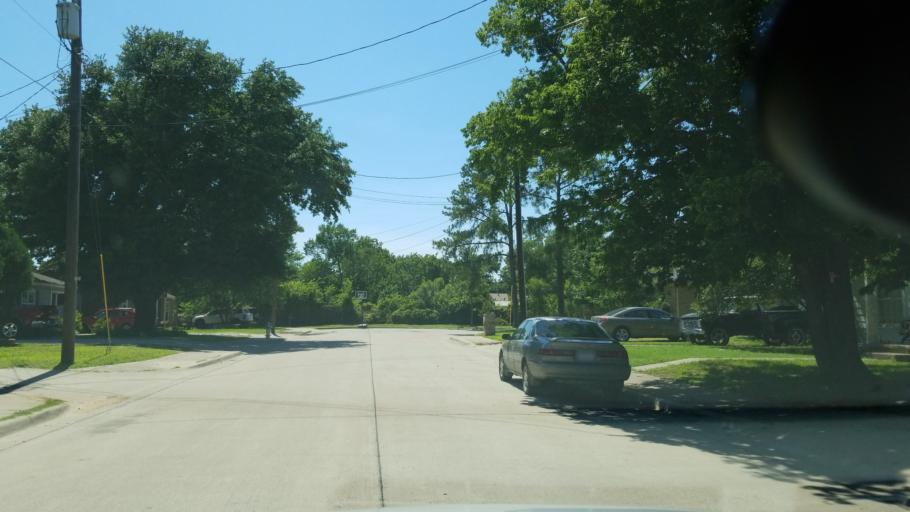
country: US
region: Texas
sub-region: Dallas County
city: Irving
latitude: 32.8304
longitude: -96.9403
